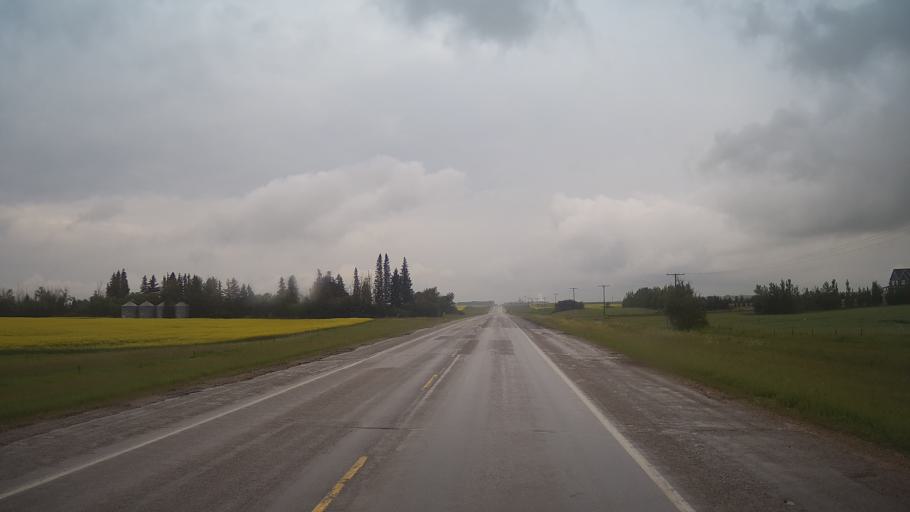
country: CA
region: Saskatchewan
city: Unity
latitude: 52.4350
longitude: -109.0358
